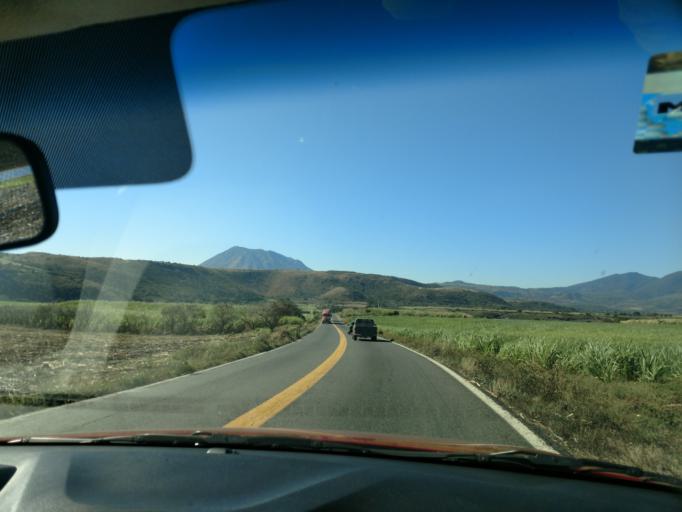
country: MX
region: Nayarit
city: San Pedro Lagunillas
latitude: 21.1501
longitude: -104.6107
